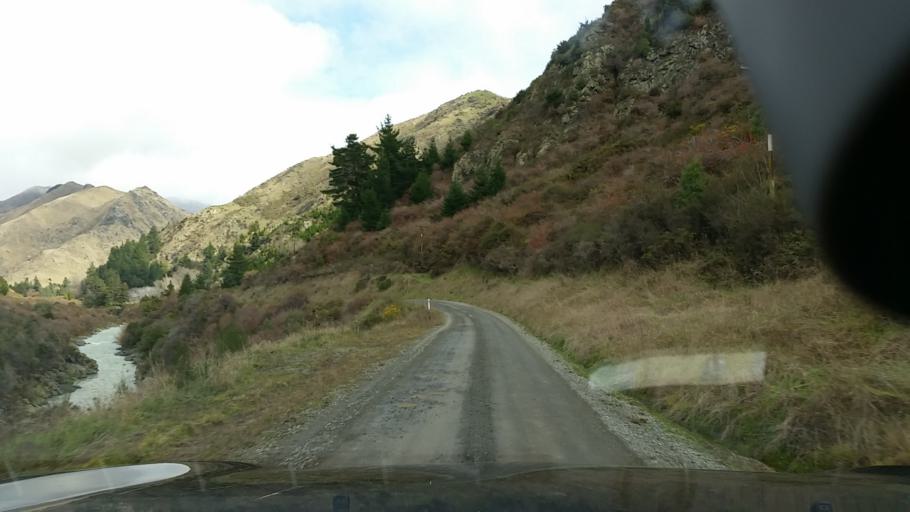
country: NZ
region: Tasman
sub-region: Tasman District
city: Richmond
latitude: -41.7151
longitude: 173.4764
